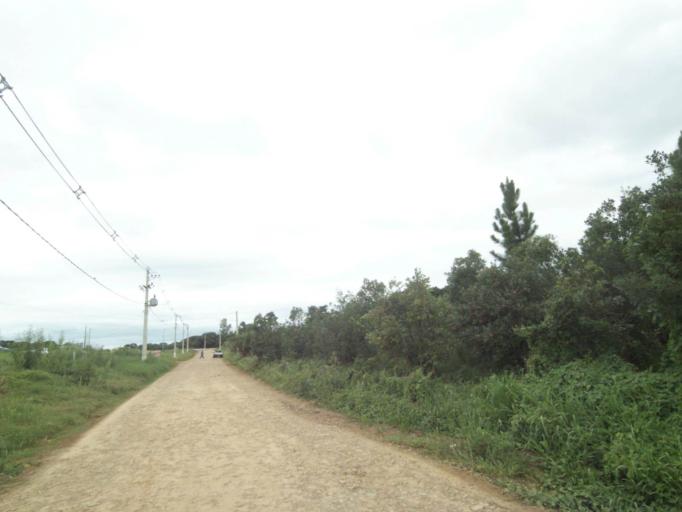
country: BR
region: Rio Grande do Sul
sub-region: Lagoa Vermelha
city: Lagoa Vermelha
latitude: -28.1899
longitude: -51.5277
